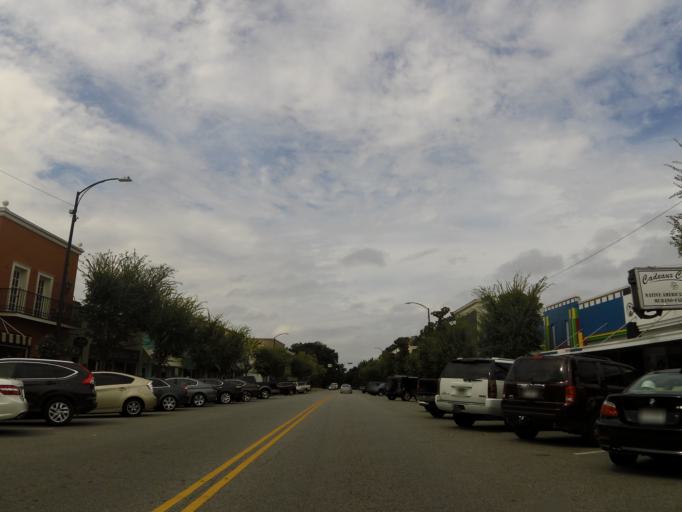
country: US
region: Alabama
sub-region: Baldwin County
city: Fairhope
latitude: 30.5231
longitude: -87.9035
